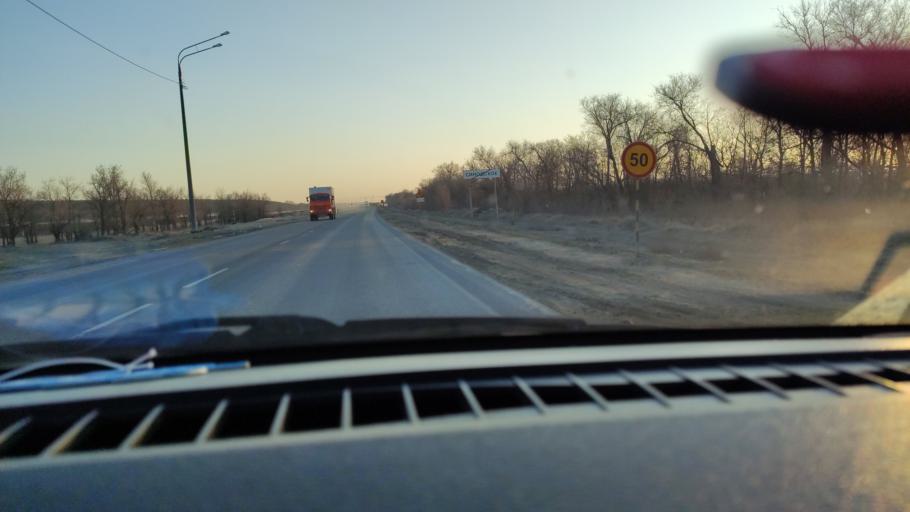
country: RU
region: Saratov
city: Sinodskoye
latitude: 51.9992
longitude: 46.6766
